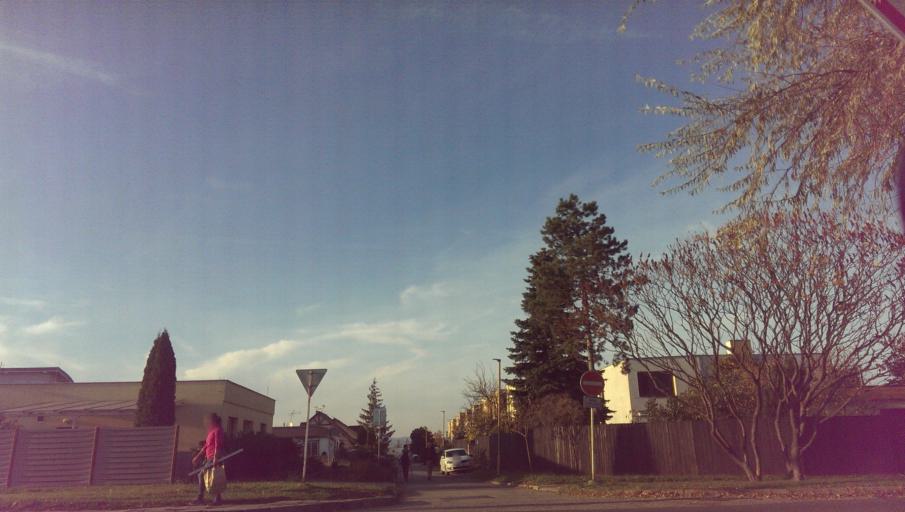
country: CZ
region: Zlin
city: Kunovice
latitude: 49.0599
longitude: 17.4789
